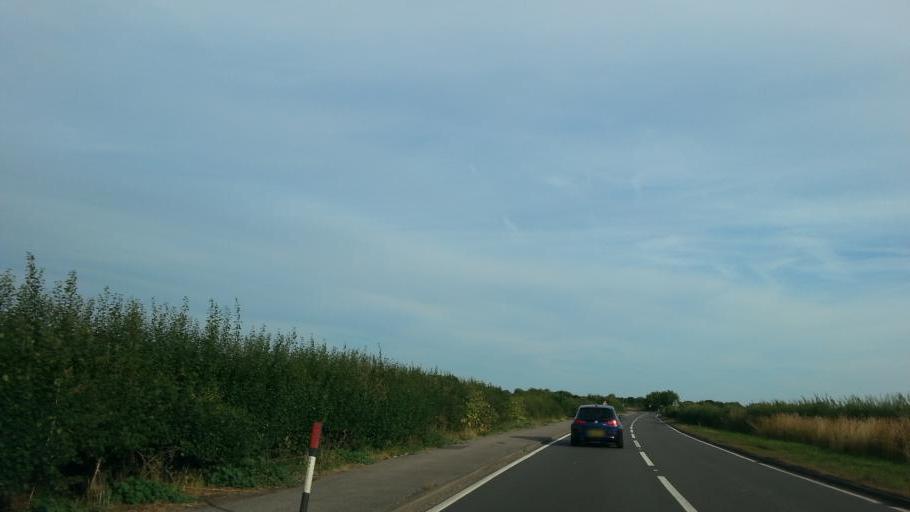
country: GB
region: England
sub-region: Nottinghamshire
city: Newark on Trent
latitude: 53.0865
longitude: -0.8349
